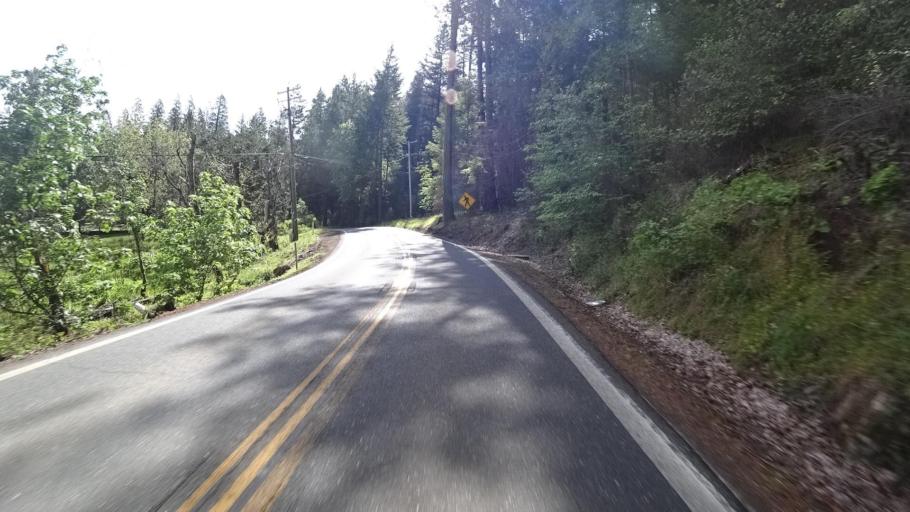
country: US
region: California
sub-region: Lake County
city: Cobb
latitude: 38.8755
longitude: -122.7301
